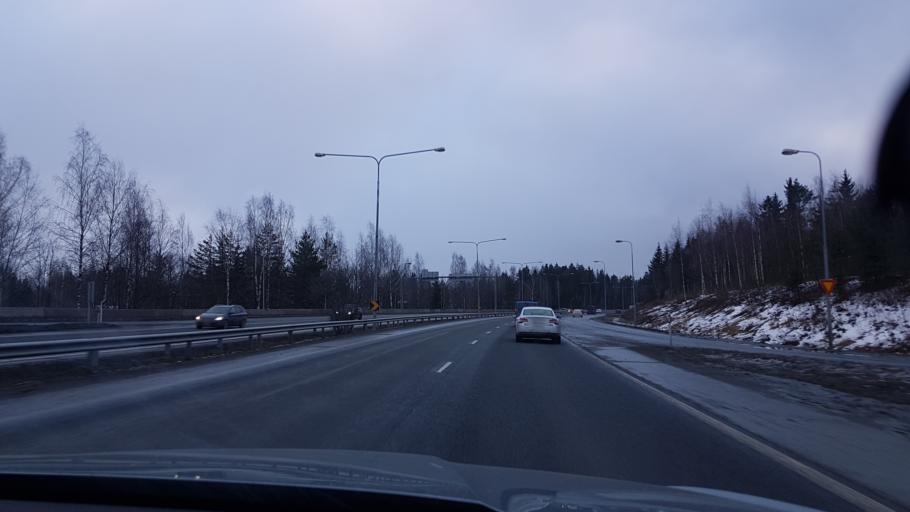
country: FI
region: Pirkanmaa
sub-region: Tampere
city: Tampere
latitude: 61.4174
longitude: 23.7623
